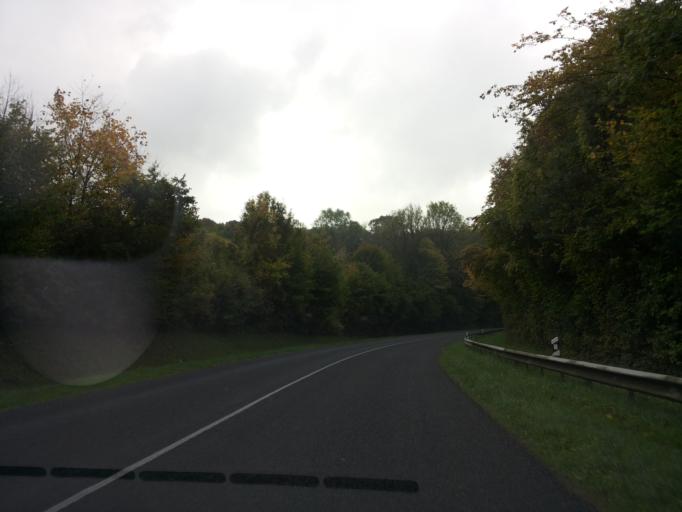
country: FR
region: Lorraine
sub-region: Departement de la Meuse
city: Montmedy
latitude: 49.4964
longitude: 5.3916
